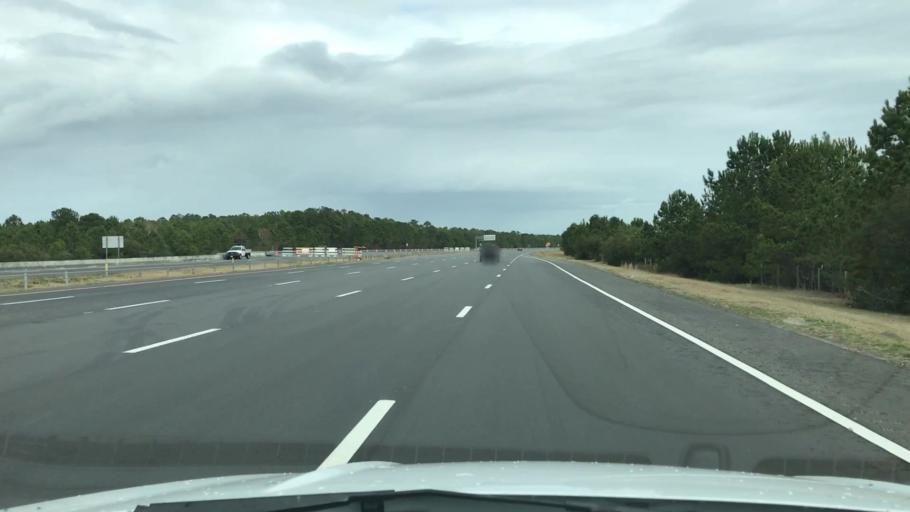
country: US
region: South Carolina
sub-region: Horry County
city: Socastee
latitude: 33.7058
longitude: -79.0116
